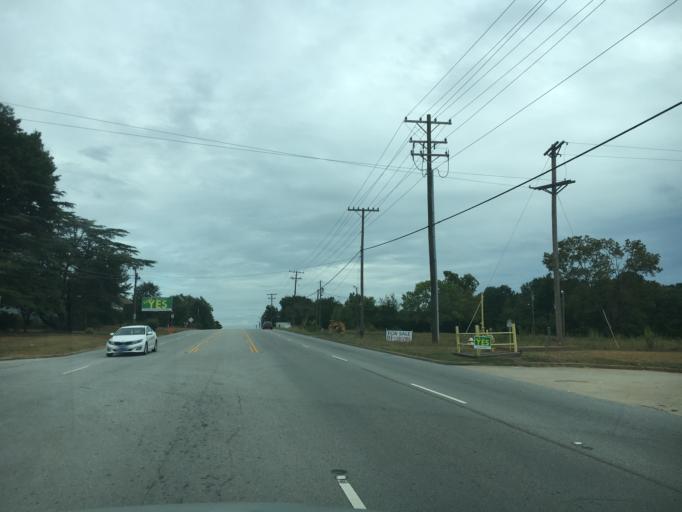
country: US
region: South Carolina
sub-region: Laurens County
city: Watts Mills
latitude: 34.4916
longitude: -81.9761
